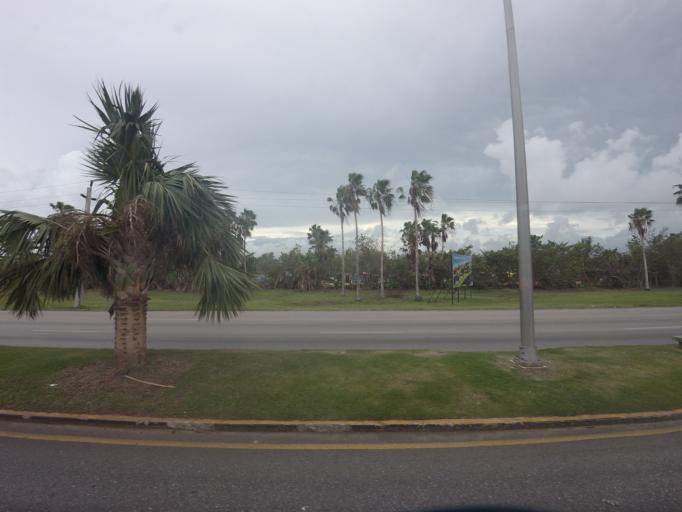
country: CU
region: Matanzas
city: Varadero
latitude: 23.1372
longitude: -81.2773
